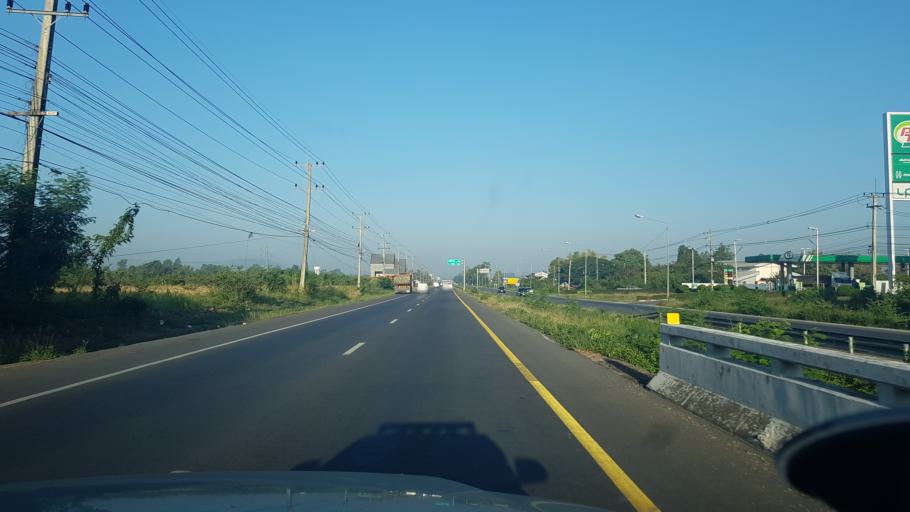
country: TH
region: Khon Kaen
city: Chum Phae
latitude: 16.5799
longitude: 102.0203
